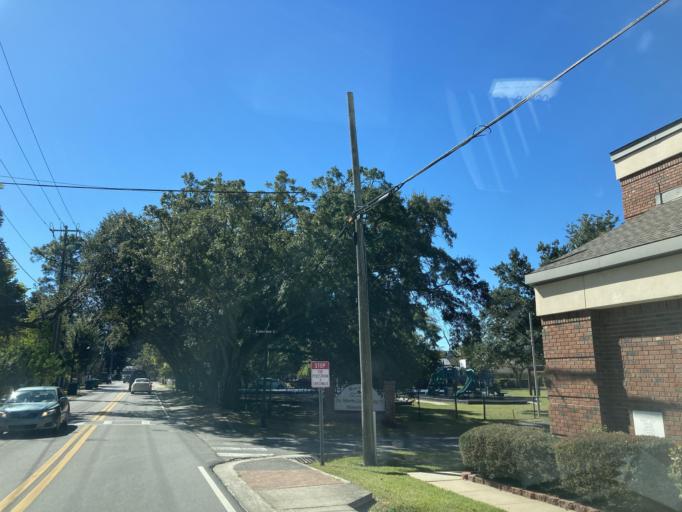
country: US
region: Mississippi
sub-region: Jackson County
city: Ocean Springs
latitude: 30.4150
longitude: -88.8186
